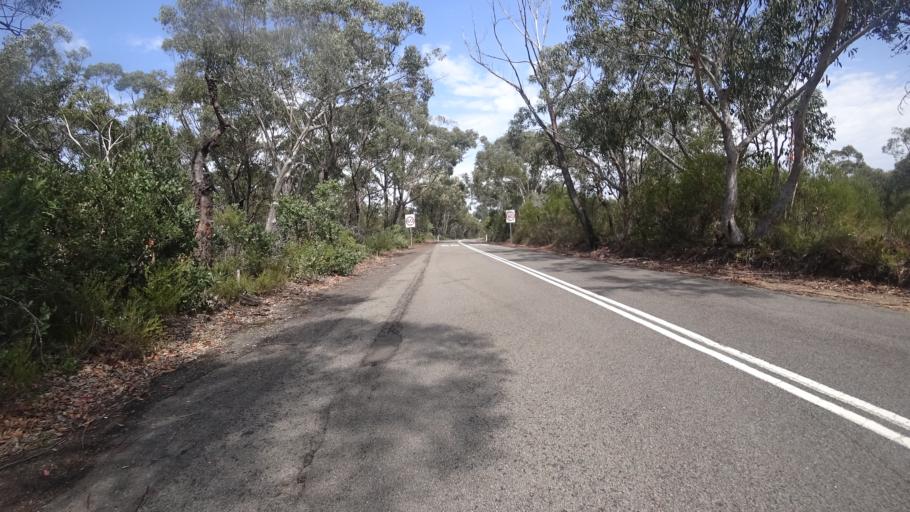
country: AU
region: New South Wales
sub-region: Hornsby Shire
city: Mount Colah
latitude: -33.6777
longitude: 151.1276
